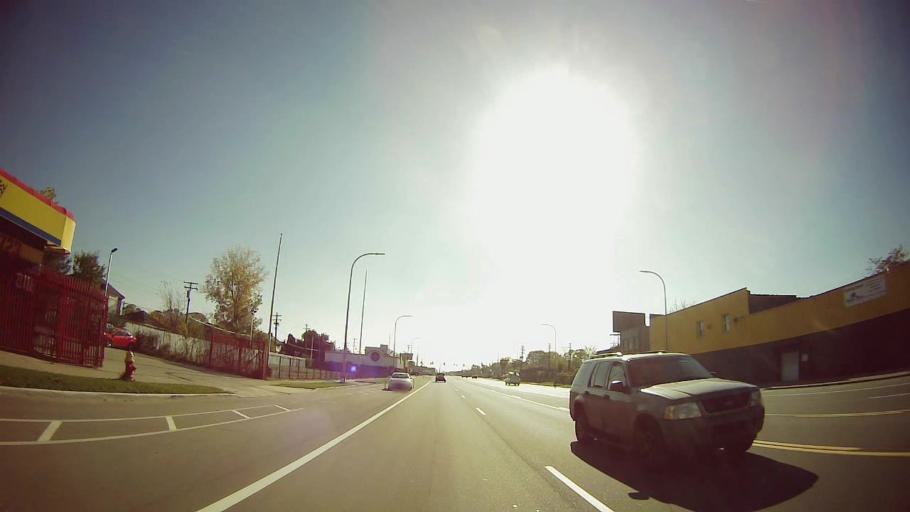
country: US
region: Michigan
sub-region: Wayne County
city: Dearborn
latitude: 42.3537
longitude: -83.1367
